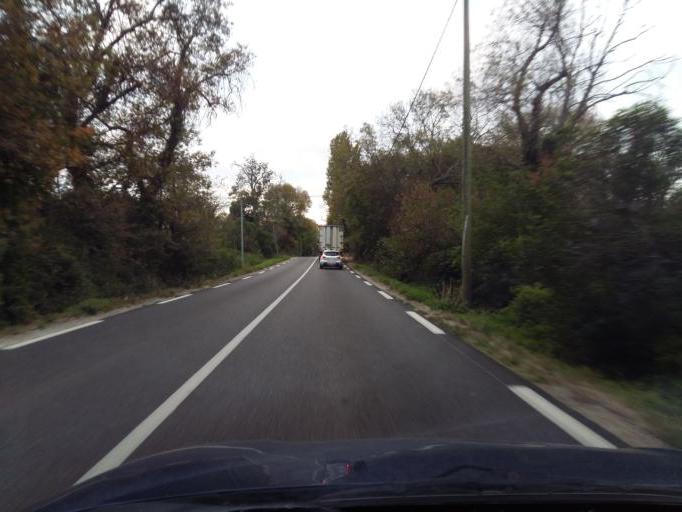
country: FR
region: Provence-Alpes-Cote d'Azur
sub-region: Departement des Bouches-du-Rhone
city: Miramas
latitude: 43.6141
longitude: 5.0124
